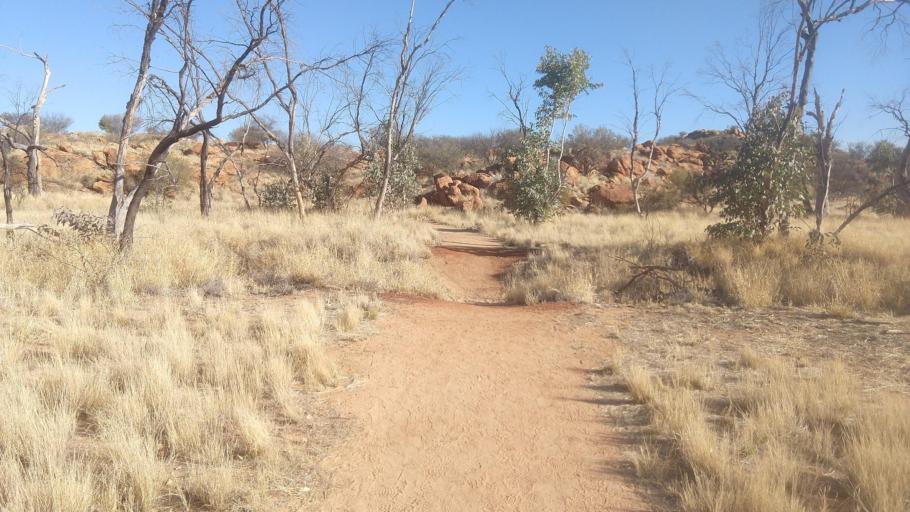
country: AU
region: Northern Territory
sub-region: Alice Springs
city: Alice Springs
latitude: -23.6687
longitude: 133.8833
